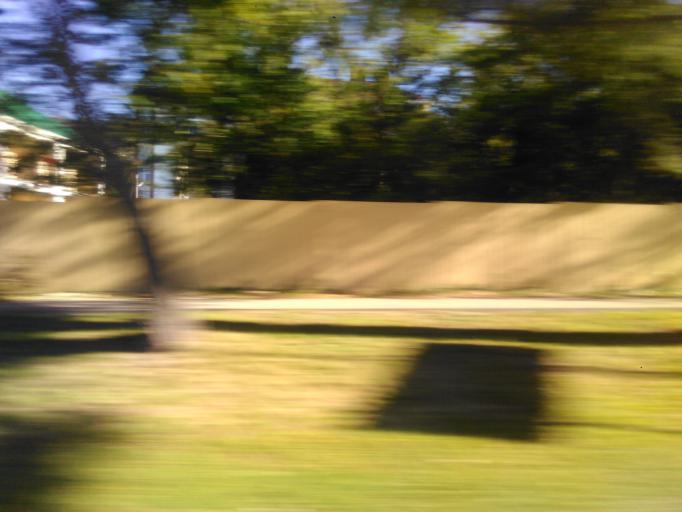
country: RU
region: Krasnodarskiy
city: Gelendzhik
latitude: 44.5828
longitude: 38.0621
